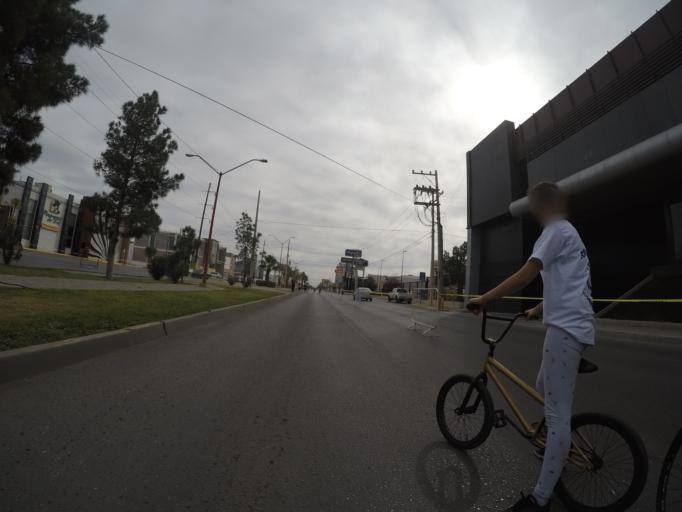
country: MX
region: Chihuahua
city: Ciudad Juarez
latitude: 31.7314
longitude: -106.4115
